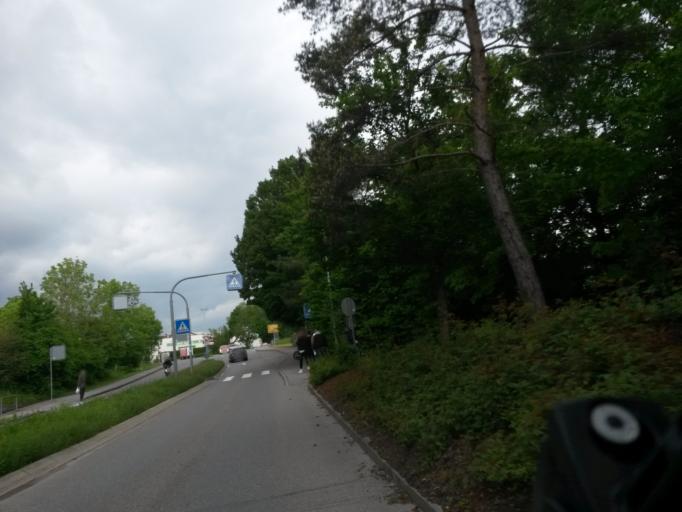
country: DE
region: Baden-Wuerttemberg
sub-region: Tuebingen Region
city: Bad Waldsee
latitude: 47.9260
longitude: 9.7590
